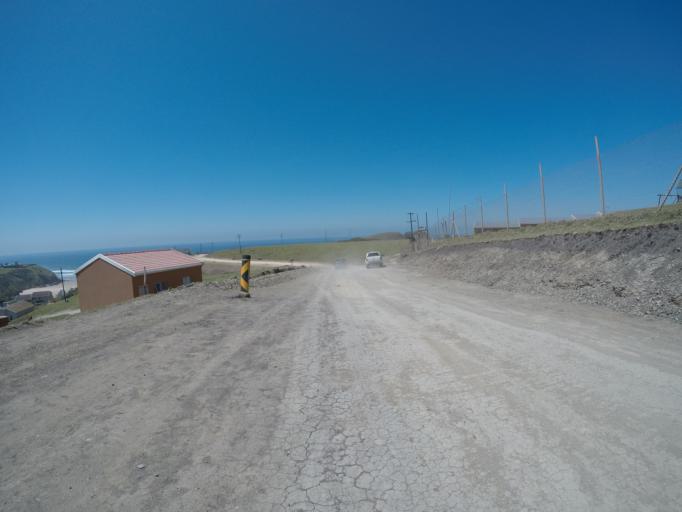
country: ZA
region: Eastern Cape
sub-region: OR Tambo District Municipality
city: Libode
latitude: -32.0334
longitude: 29.1071
